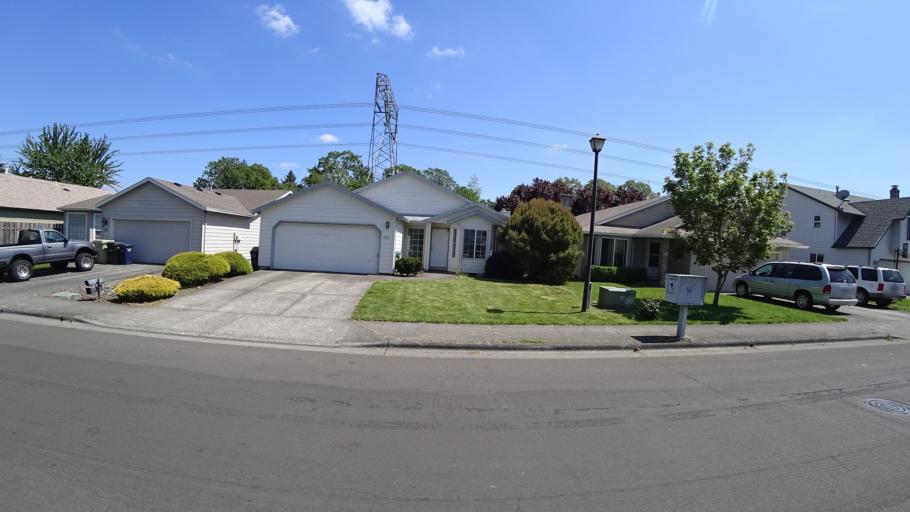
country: US
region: Oregon
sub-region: Washington County
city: Aloha
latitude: 45.5132
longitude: -122.8978
